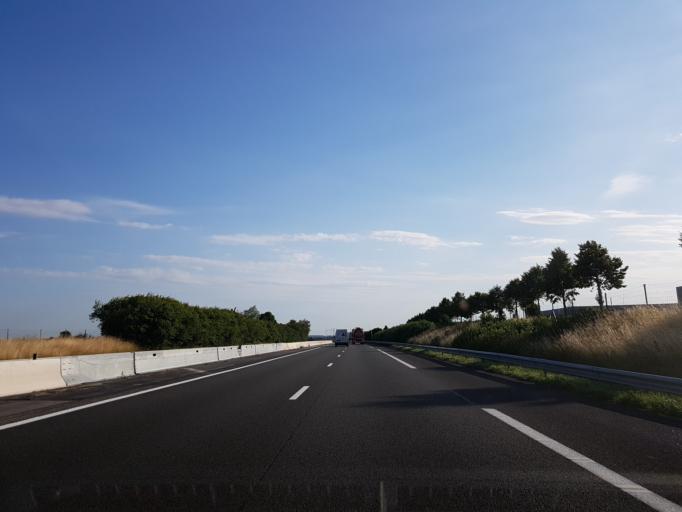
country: FR
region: Nord-Pas-de-Calais
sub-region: Departement du Nord
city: Neuville-Saint-Remy
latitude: 50.1911
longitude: 3.1983
